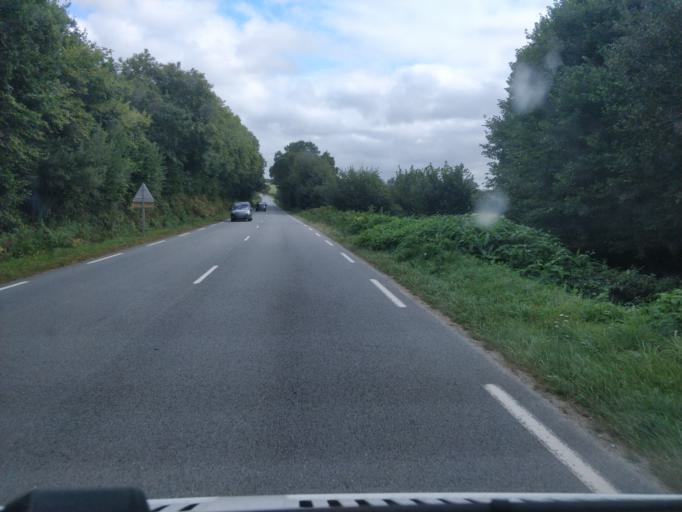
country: FR
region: Brittany
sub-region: Departement du Finistere
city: Pluguffan
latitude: 47.9936
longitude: -4.2059
